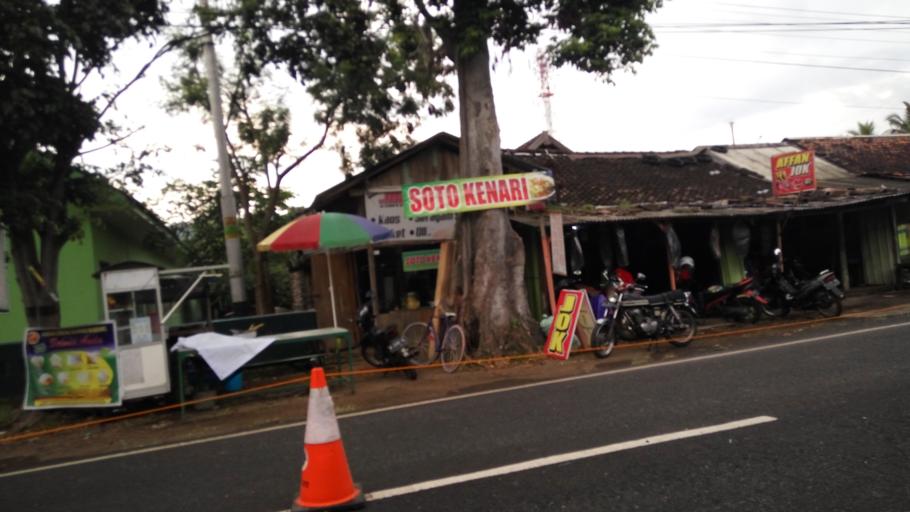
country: ID
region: Central Java
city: Ambarawa
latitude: -7.2674
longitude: 110.4037
